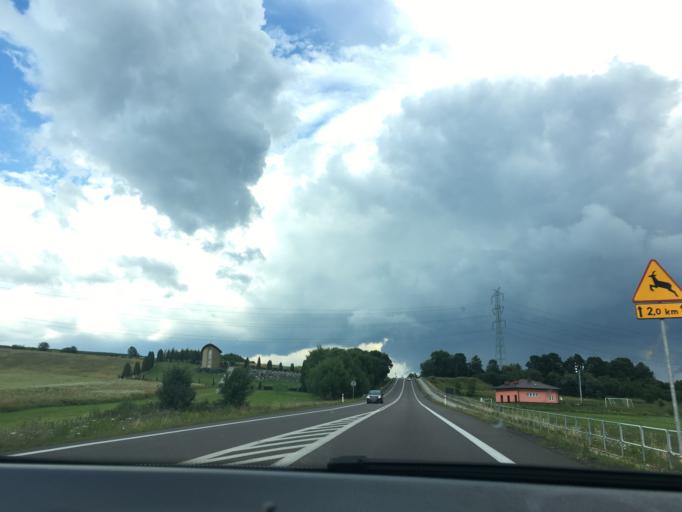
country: PL
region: Subcarpathian Voivodeship
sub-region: Powiat krosnienski
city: Kroscienko Wyzne
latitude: 49.6855
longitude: 21.8593
